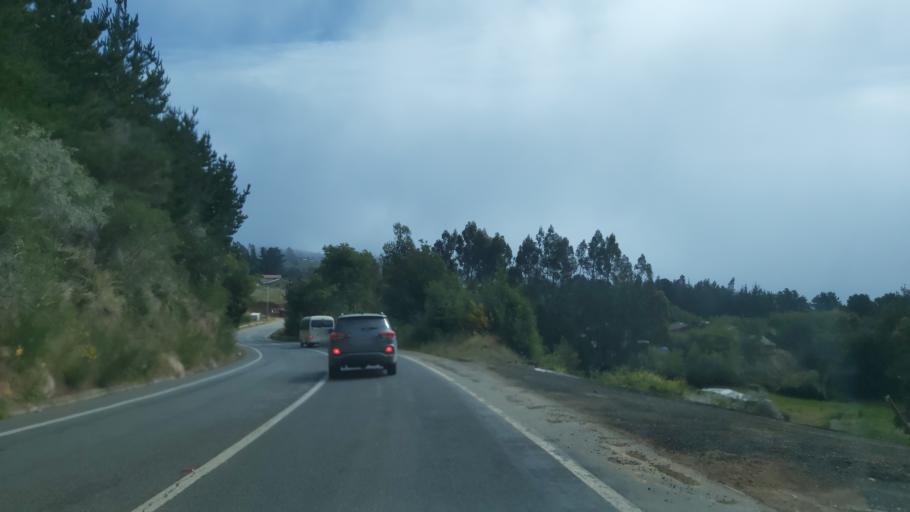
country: CL
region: Maule
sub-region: Provincia de Cauquenes
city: Cauquenes
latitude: -35.8688
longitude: -72.6544
